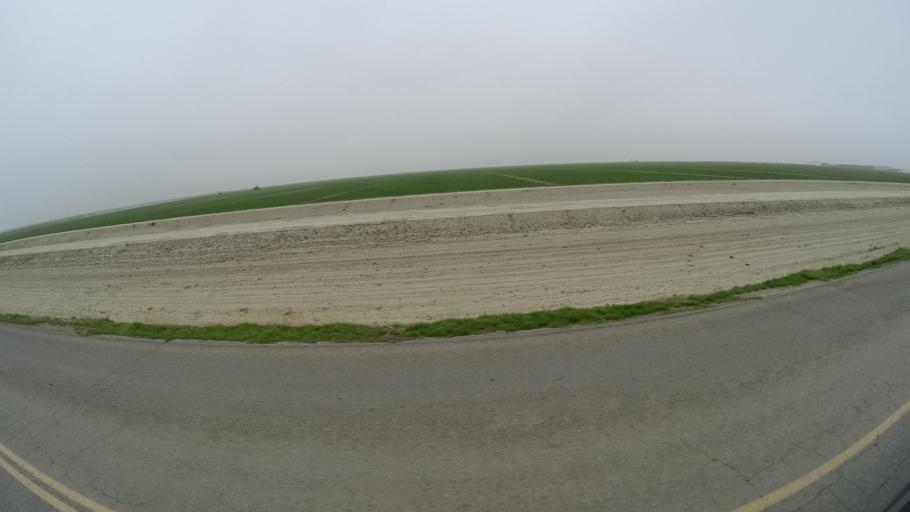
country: US
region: California
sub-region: Kern County
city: Rosedale
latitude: 35.2101
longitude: -119.2241
